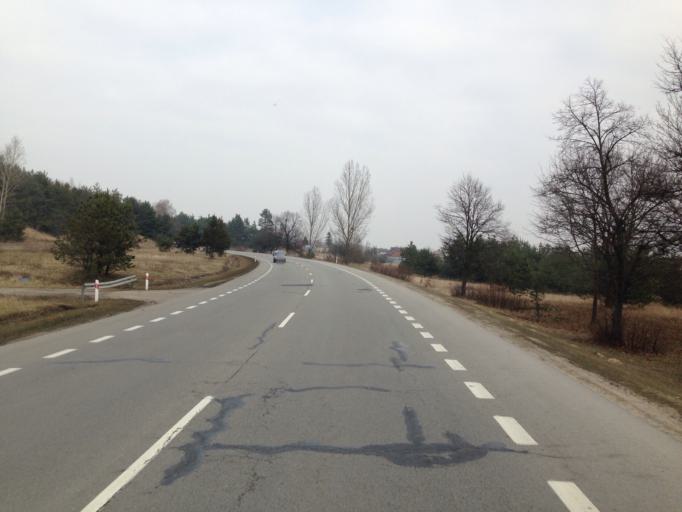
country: PL
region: Pomeranian Voivodeship
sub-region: Powiat tczewski
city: Gniew
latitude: 53.8188
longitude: 18.8113
